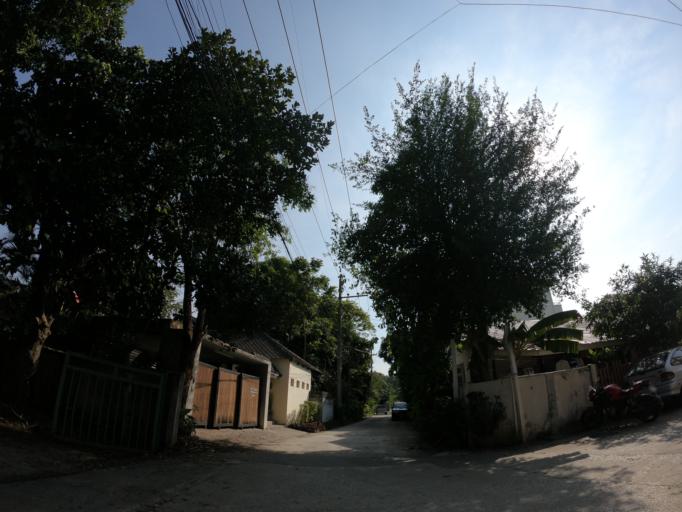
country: TH
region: Chiang Mai
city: Chiang Mai
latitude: 18.8248
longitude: 98.9904
